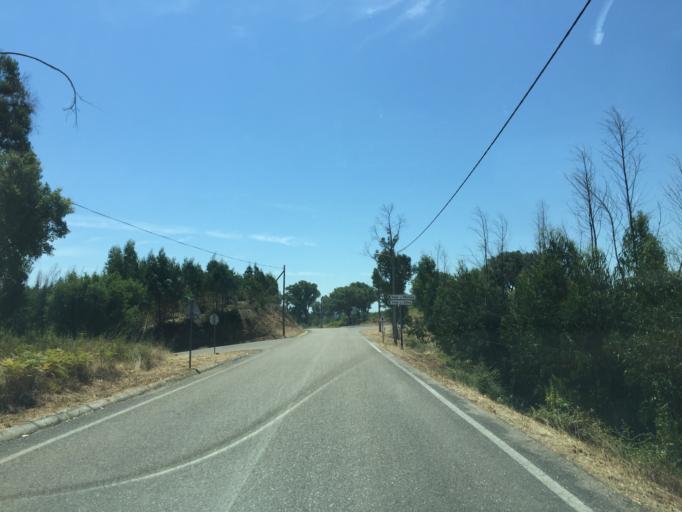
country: PT
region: Santarem
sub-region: Tomar
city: Tomar
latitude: 39.5791
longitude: -8.2975
